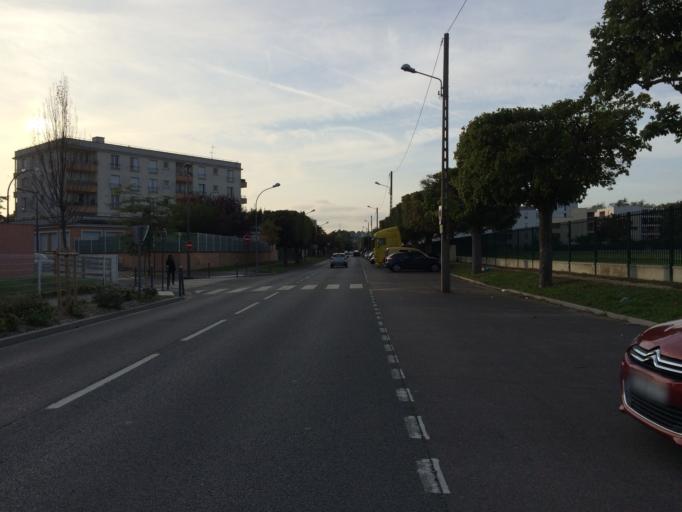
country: FR
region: Ile-de-France
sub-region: Departement de l'Essonne
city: Vigneux-sur-Seine
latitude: 48.7071
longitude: 2.4205
